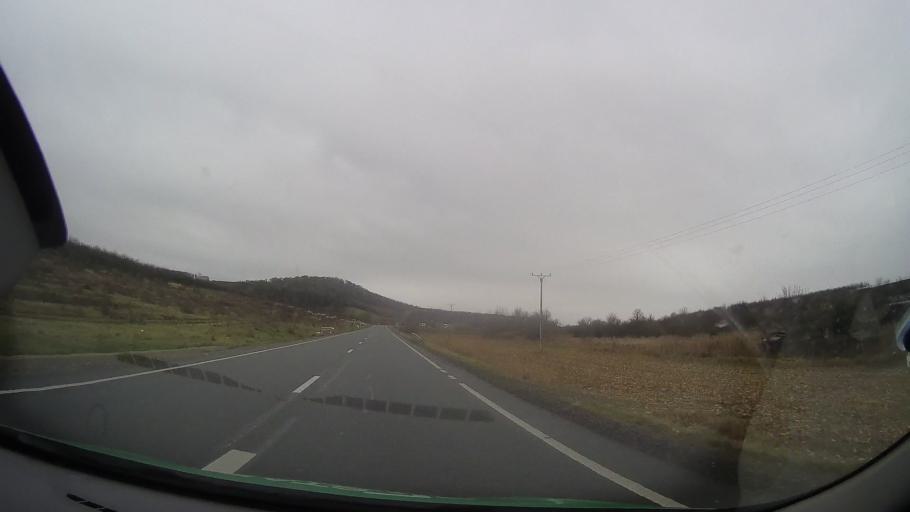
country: RO
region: Mures
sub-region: Comuna Breaza
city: Breaza
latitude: 46.7825
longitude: 24.6528
